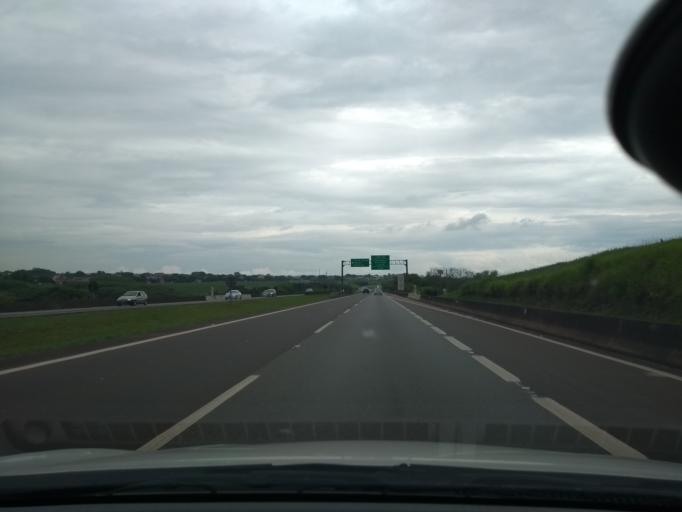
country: BR
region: Sao Paulo
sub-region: Limeira
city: Limeira
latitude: -22.5591
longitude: -47.4597
